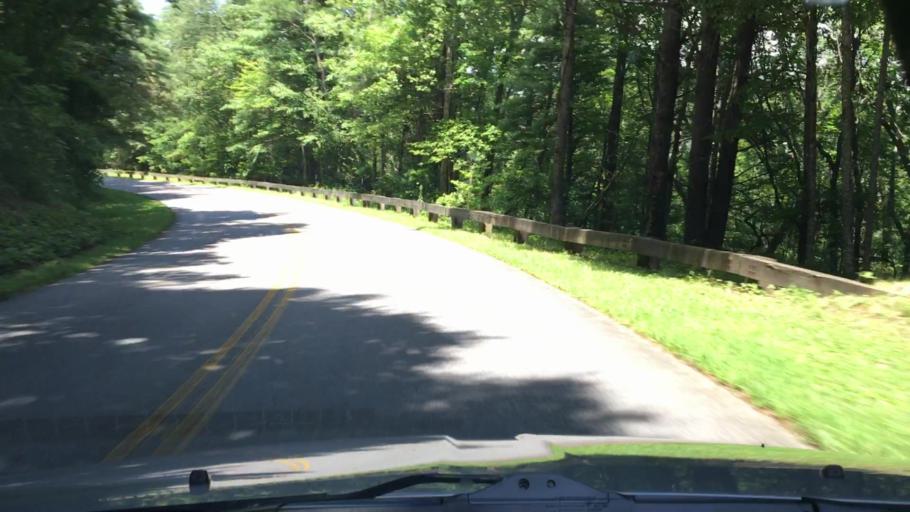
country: US
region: North Carolina
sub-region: Buncombe County
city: Asheville
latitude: 35.6387
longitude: -82.4903
